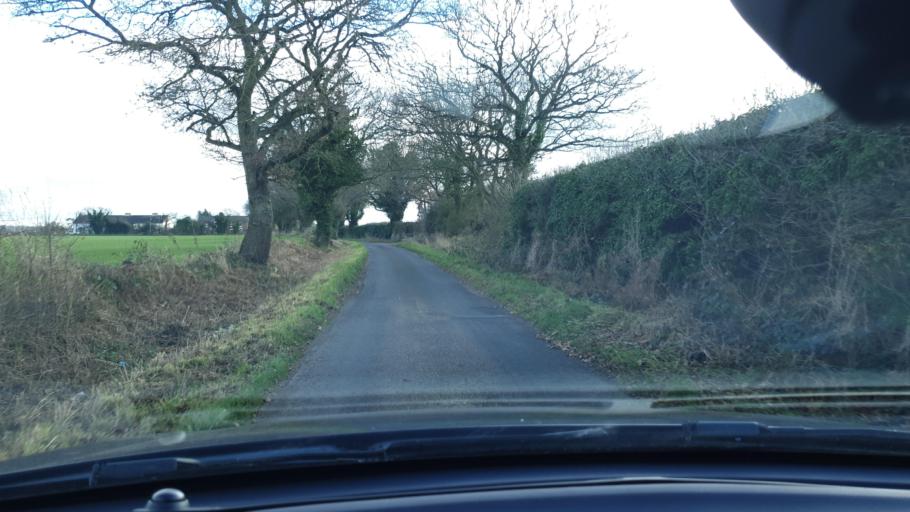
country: GB
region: England
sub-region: Essex
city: Great Bentley
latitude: 51.8533
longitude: 1.0385
